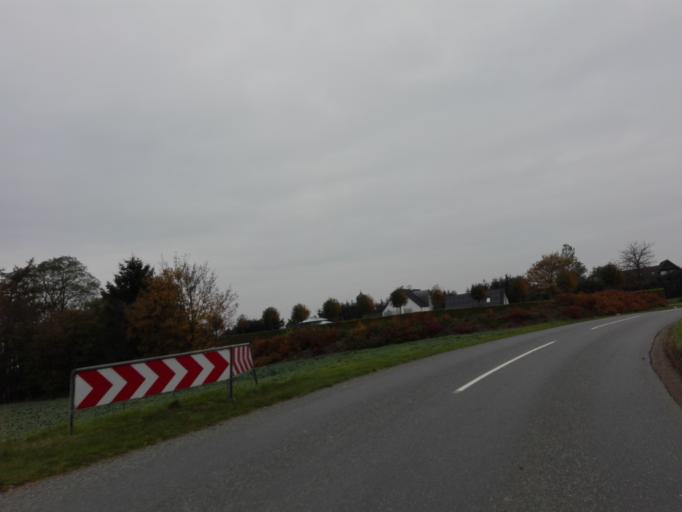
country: DK
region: Central Jutland
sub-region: Arhus Kommune
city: Beder
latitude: 56.0445
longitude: 10.2393
